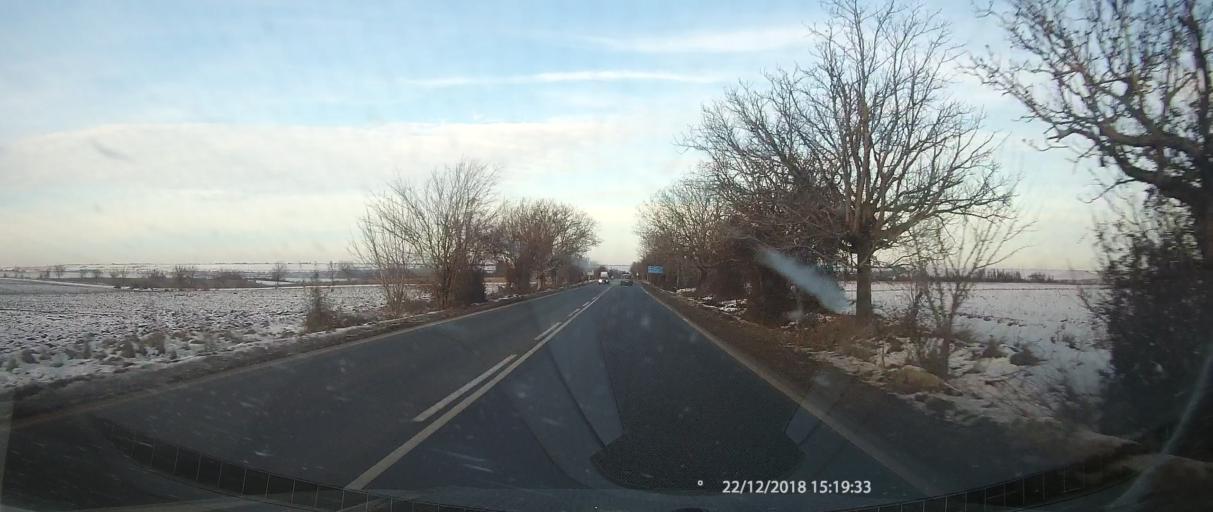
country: BG
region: Ruse
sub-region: Obshtina Dve Mogili
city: Dve Mogili
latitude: 43.6581
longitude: 25.8766
